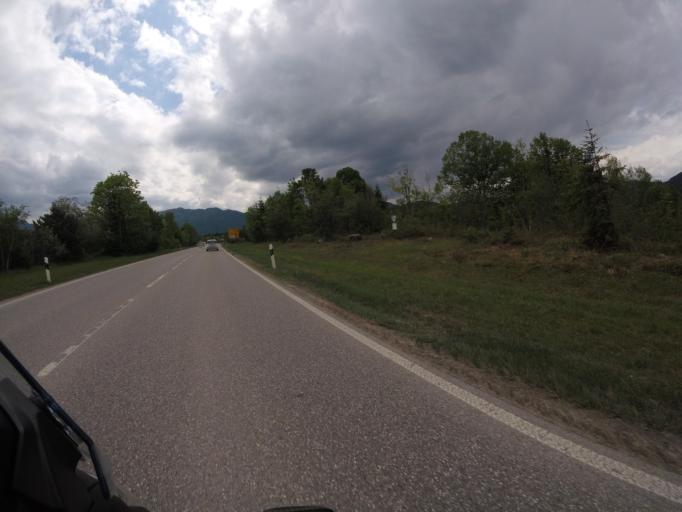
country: DE
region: Bavaria
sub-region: Upper Bavaria
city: Lenggries
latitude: 47.6631
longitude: 11.5836
